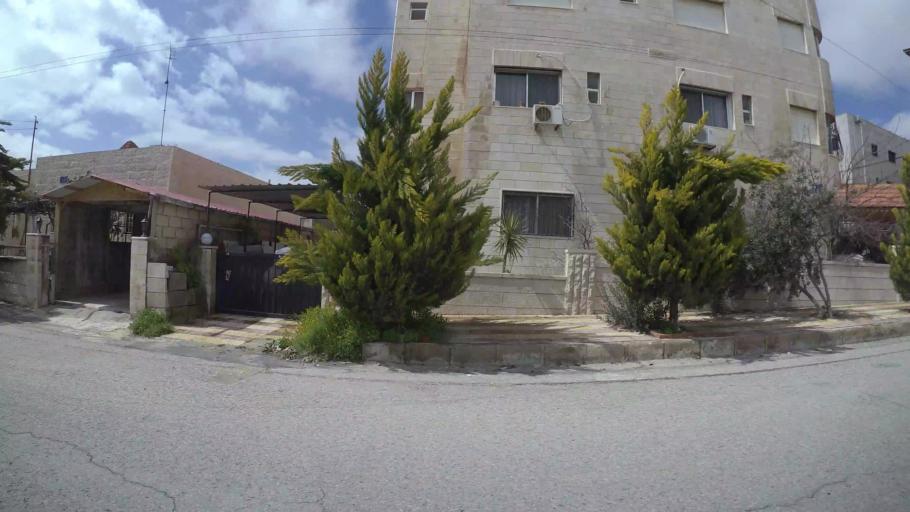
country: JO
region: Amman
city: Al Jubayhah
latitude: 31.9935
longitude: 35.8525
